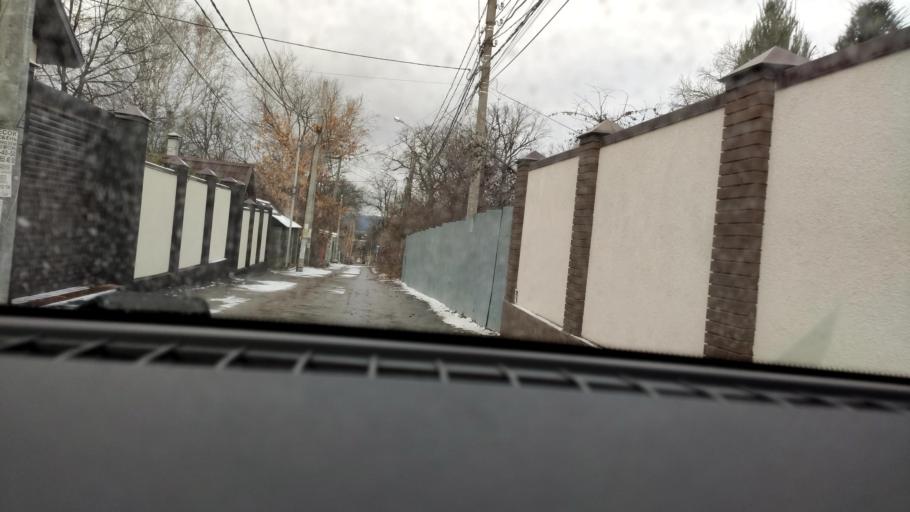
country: RU
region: Samara
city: Samara
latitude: 53.2730
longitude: 50.1994
